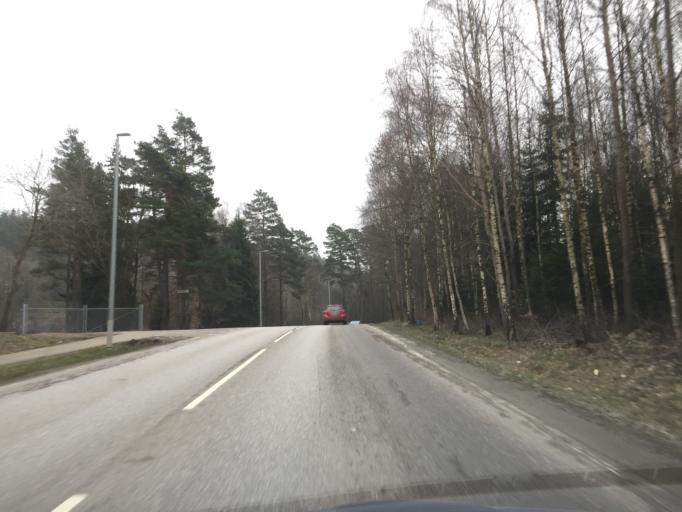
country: SE
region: Vaestra Goetaland
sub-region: Goteborg
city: Rannebergen
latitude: 57.7698
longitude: 12.0747
